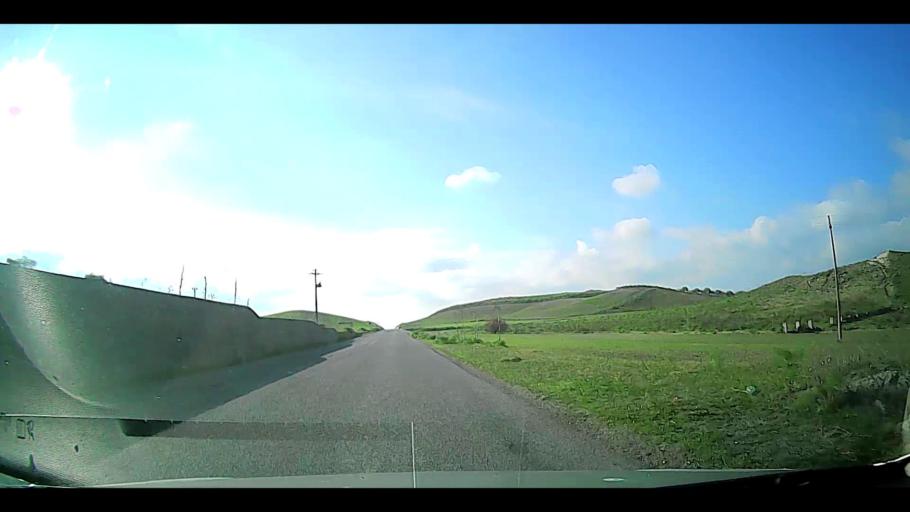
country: IT
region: Calabria
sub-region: Provincia di Crotone
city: Rocca di Neto
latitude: 39.1948
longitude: 17.0594
